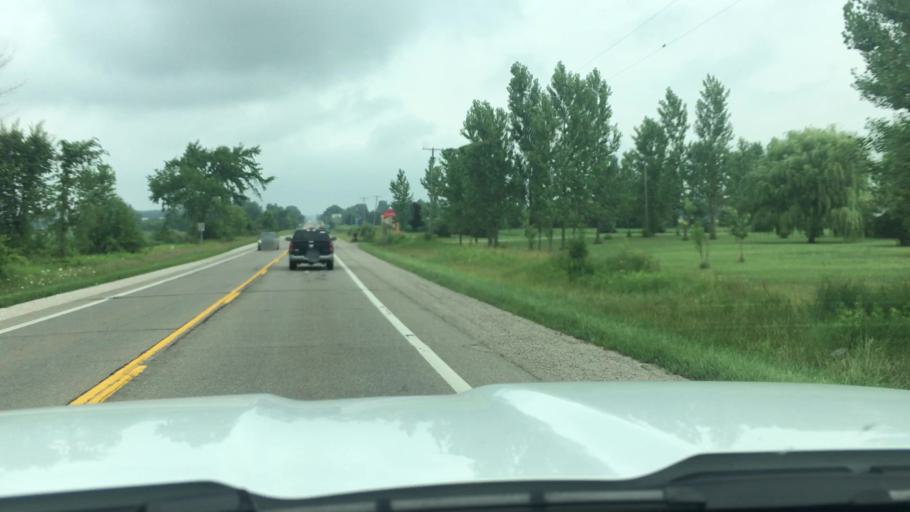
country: US
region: Michigan
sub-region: Sanilac County
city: Brown City
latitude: 43.2013
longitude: -83.0770
